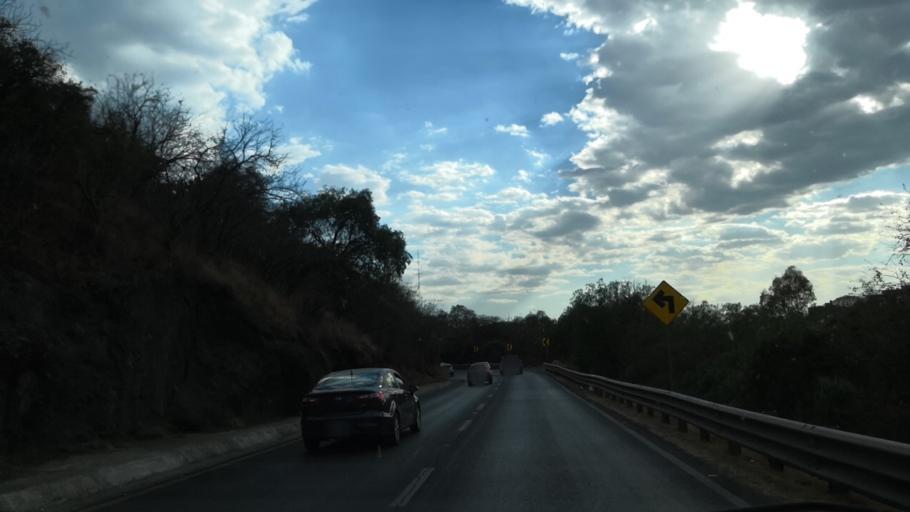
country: MX
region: Guanajuato
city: Marfil
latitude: 21.0035
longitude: -101.2811
